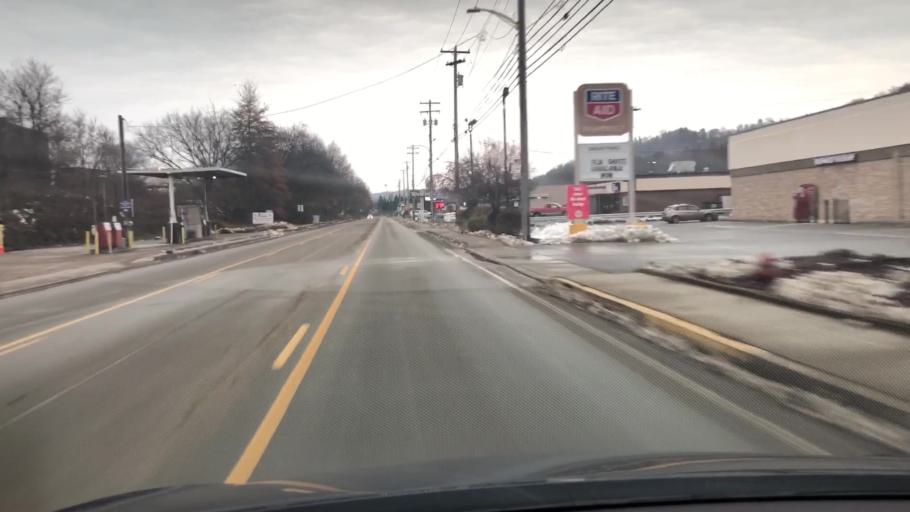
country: US
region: Pennsylvania
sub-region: Clarion County
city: Clarion
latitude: 41.0022
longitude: -79.3269
